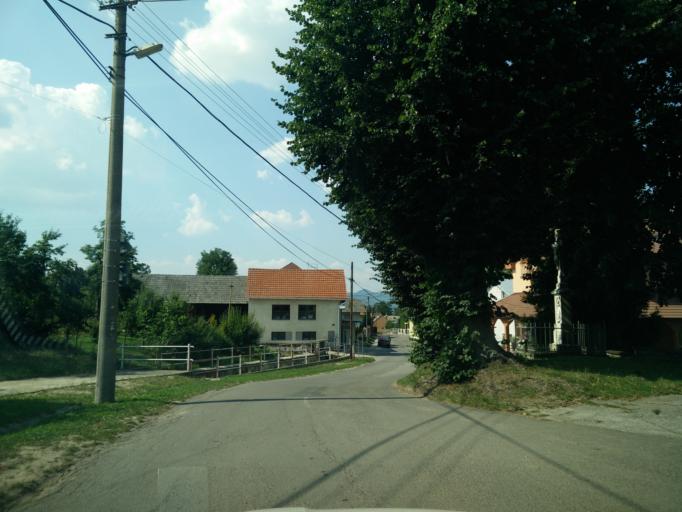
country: SK
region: Zilinsky
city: Rajec
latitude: 49.0624
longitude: 18.6540
